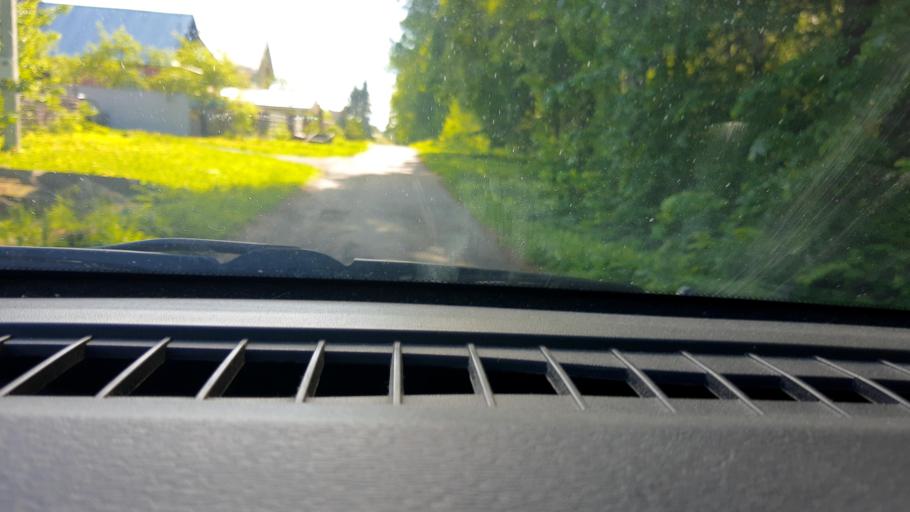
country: RU
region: Nizjnij Novgorod
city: Afonino
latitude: 56.1995
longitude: 44.0301
